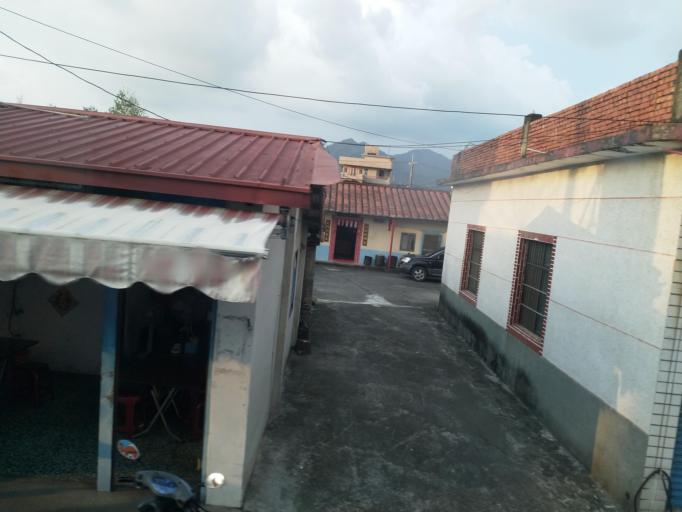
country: TW
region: Taiwan
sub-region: Pingtung
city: Pingtung
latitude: 22.8868
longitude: 120.5309
